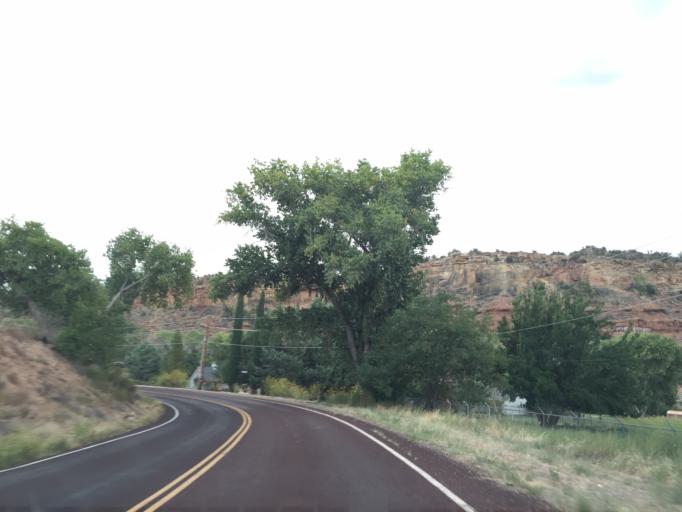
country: US
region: Utah
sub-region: Washington County
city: Hildale
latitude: 37.1604
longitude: -113.0306
